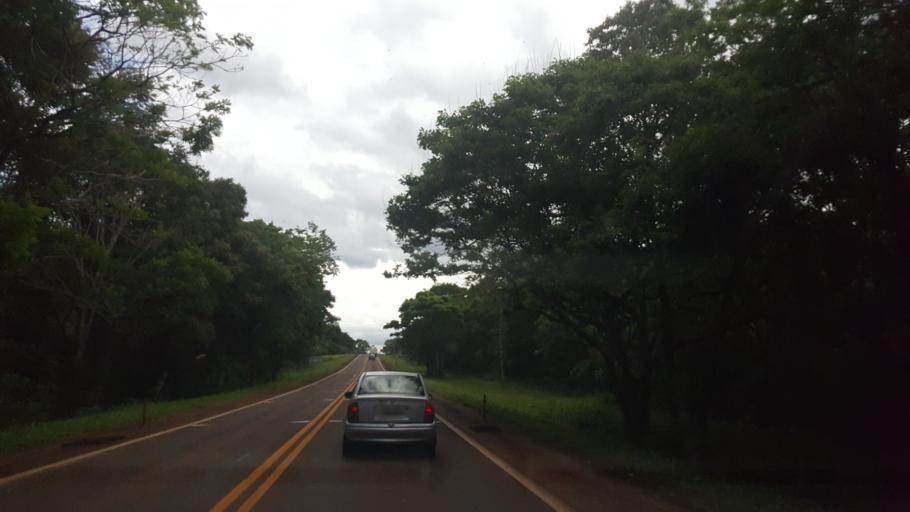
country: AR
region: Misiones
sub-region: Departamento de Iguazu
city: Puerto Iguazu
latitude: -25.7333
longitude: -54.5333
